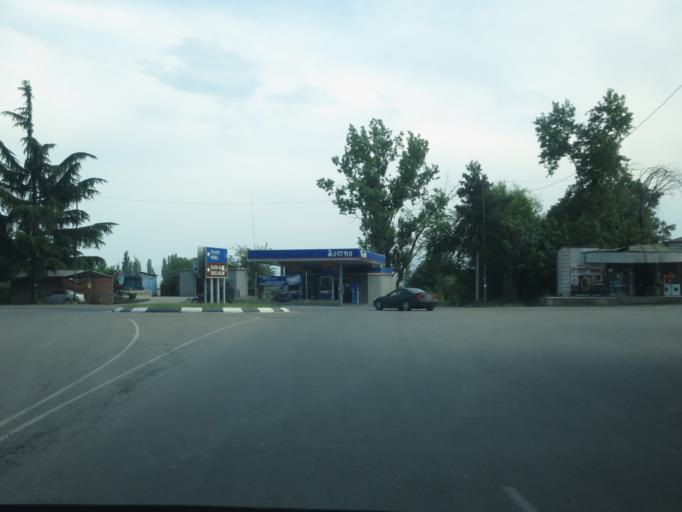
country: GE
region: Kakheti
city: Qvareli
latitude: 41.9305
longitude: 45.8237
